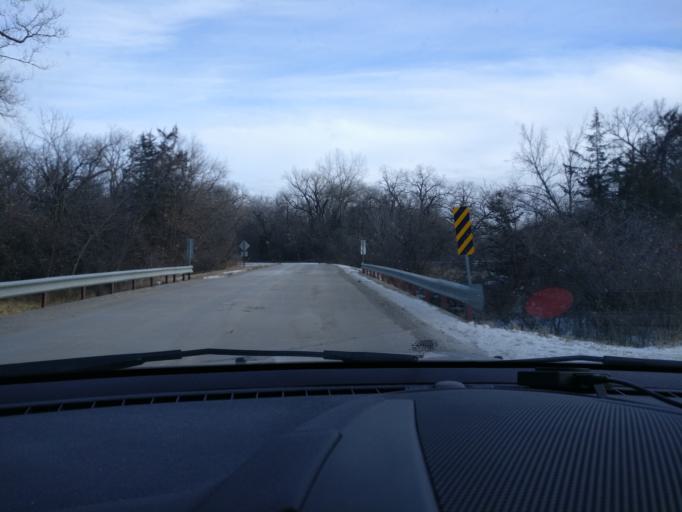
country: US
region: Nebraska
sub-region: Dodge County
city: Fremont
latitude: 41.4125
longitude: -96.5125
